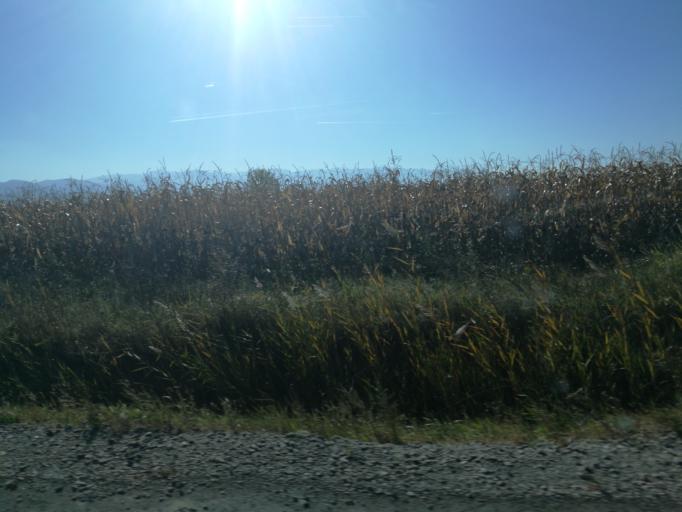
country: RO
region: Brasov
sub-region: Comuna Sinca Veche
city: Sinca Veche
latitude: 45.8004
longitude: 25.1781
